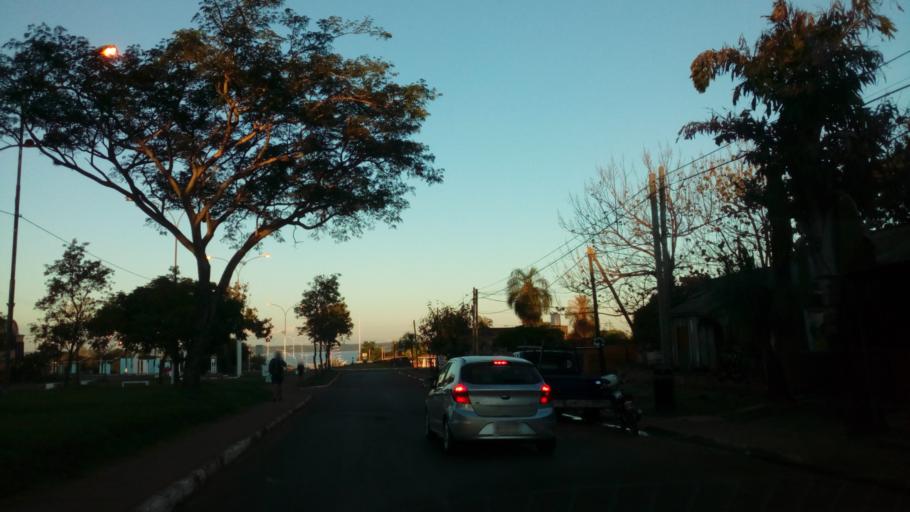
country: AR
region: Misiones
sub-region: Departamento de Capital
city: Posadas
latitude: -27.4292
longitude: -55.8807
